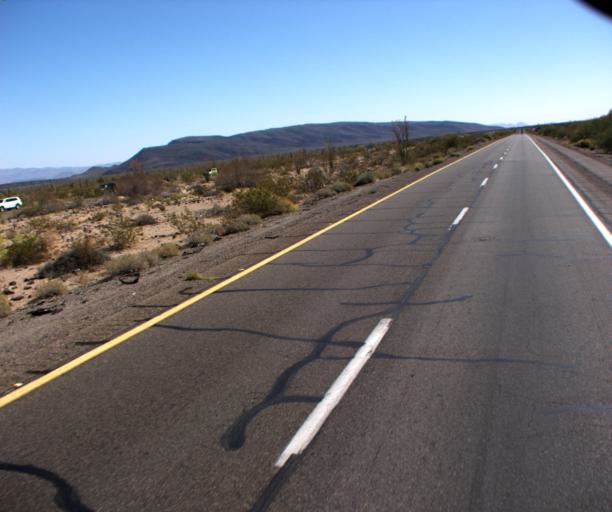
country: US
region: Arizona
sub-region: La Paz County
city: Quartzsite
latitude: 33.6571
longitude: -113.9749
